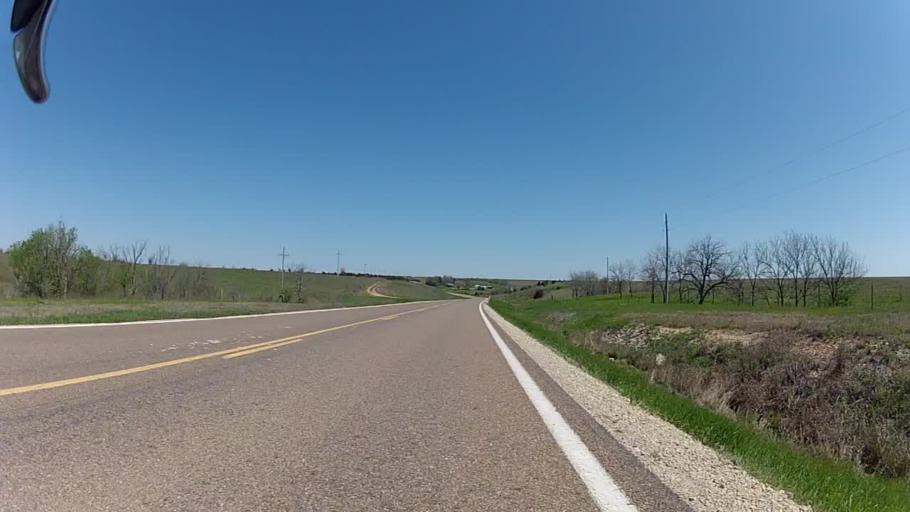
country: US
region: Kansas
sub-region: Wabaunsee County
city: Alma
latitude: 38.9181
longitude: -96.5201
